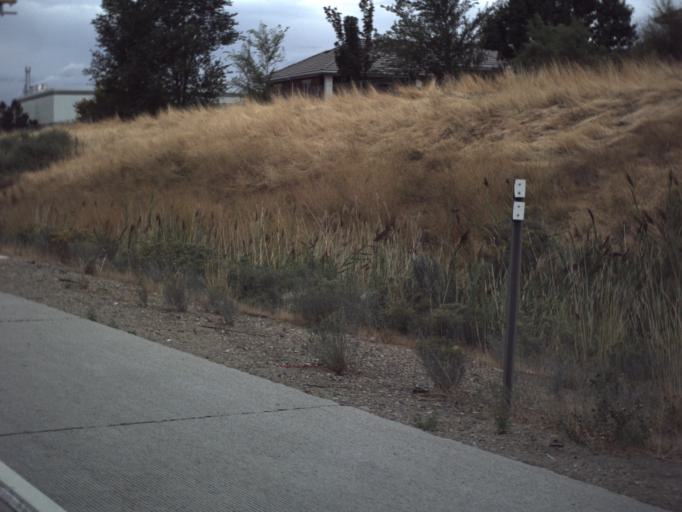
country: US
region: Utah
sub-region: Salt Lake County
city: Draper
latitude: 40.5406
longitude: -111.8935
